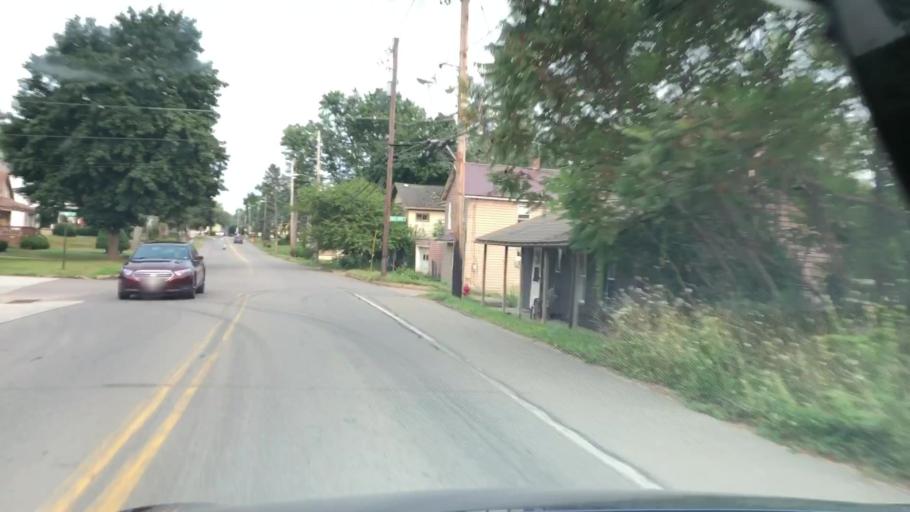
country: US
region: Pennsylvania
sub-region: Crawford County
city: Titusville
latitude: 41.6323
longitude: -79.6929
